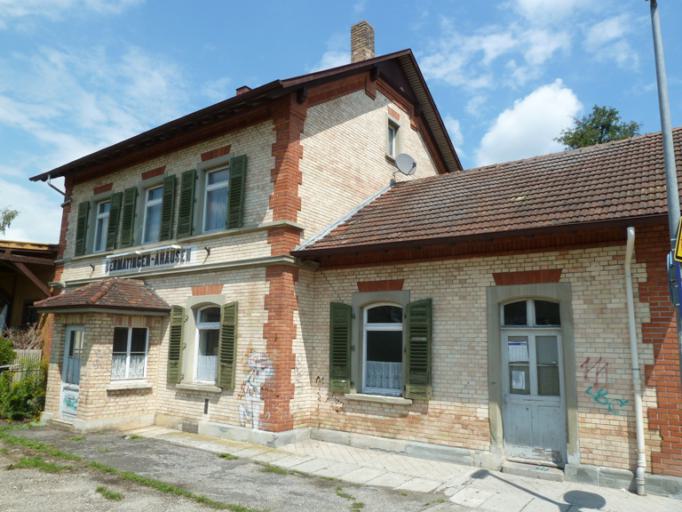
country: DE
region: Baden-Wuerttemberg
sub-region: Tuebingen Region
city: Bermatingen
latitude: 47.7306
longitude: 9.3452
